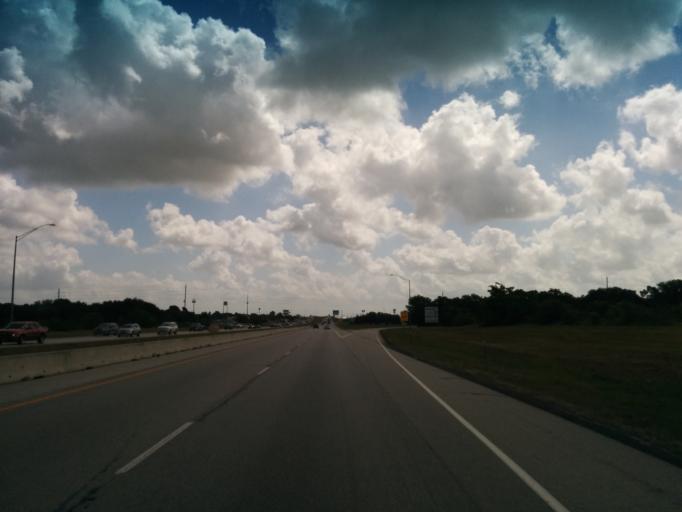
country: US
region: Texas
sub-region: Austin County
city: Sealy
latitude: 29.7616
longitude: -96.1620
